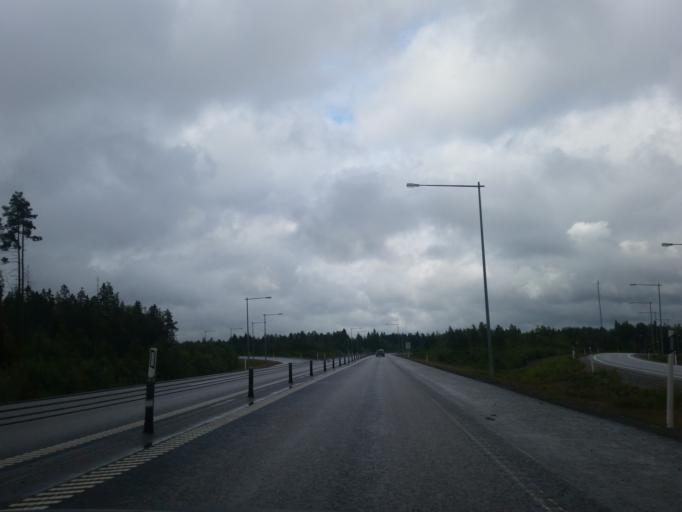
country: SE
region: Vaesterbotten
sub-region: Umea Kommun
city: Saevar
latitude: 63.8913
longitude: 20.5221
